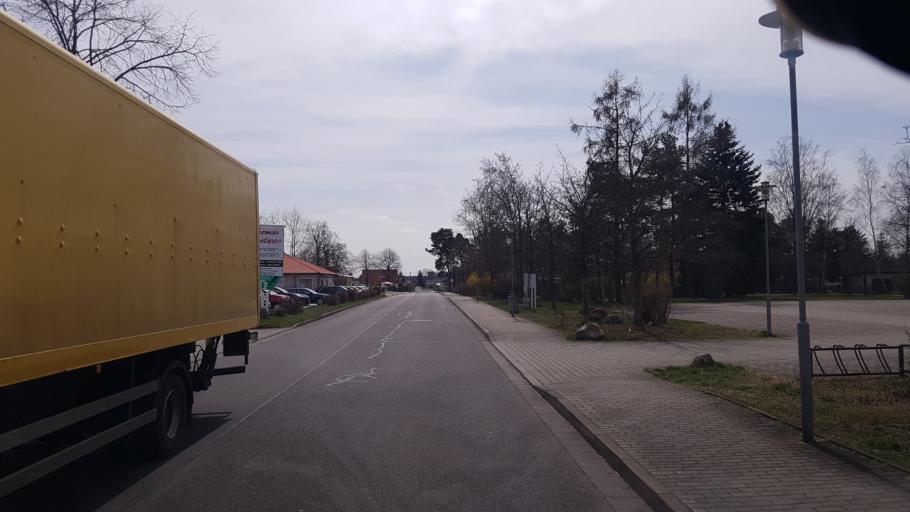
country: DE
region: Brandenburg
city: Schipkau
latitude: 51.5171
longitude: 13.8994
